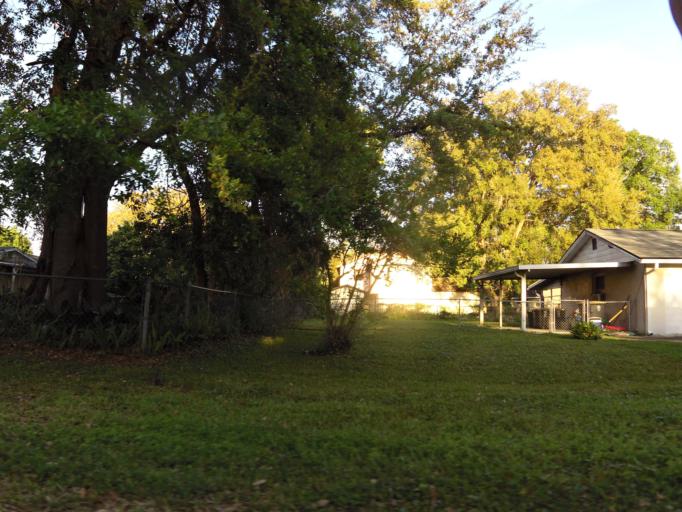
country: US
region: Florida
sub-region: Duval County
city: Jacksonville
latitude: 30.2877
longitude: -81.6477
